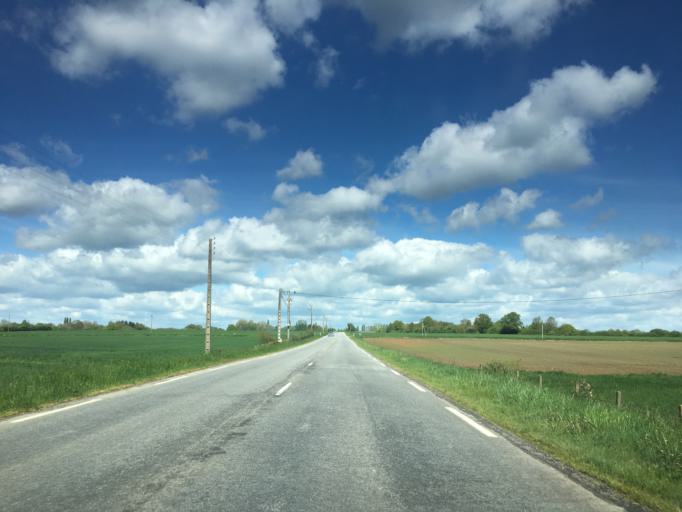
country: FR
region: Lower Normandy
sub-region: Departement de l'Orne
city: Rai
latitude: 48.8193
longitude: 0.5690
